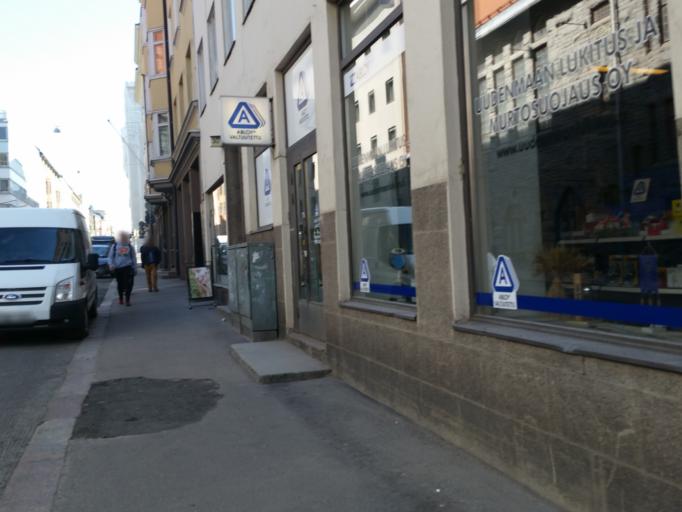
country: FI
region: Uusimaa
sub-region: Helsinki
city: Helsinki
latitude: 60.1640
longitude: 24.9316
